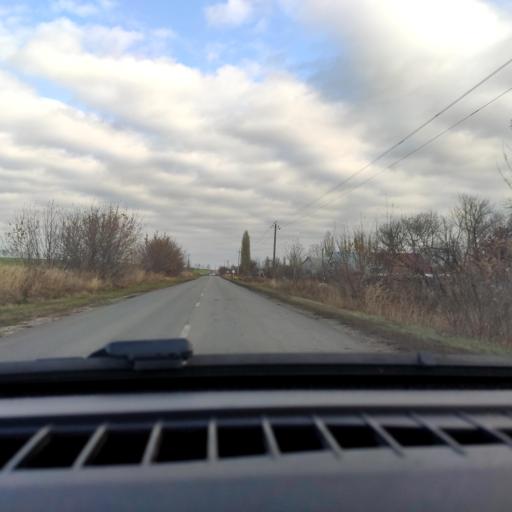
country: RU
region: Voronezj
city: Shilovo
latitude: 51.5315
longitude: 39.0353
